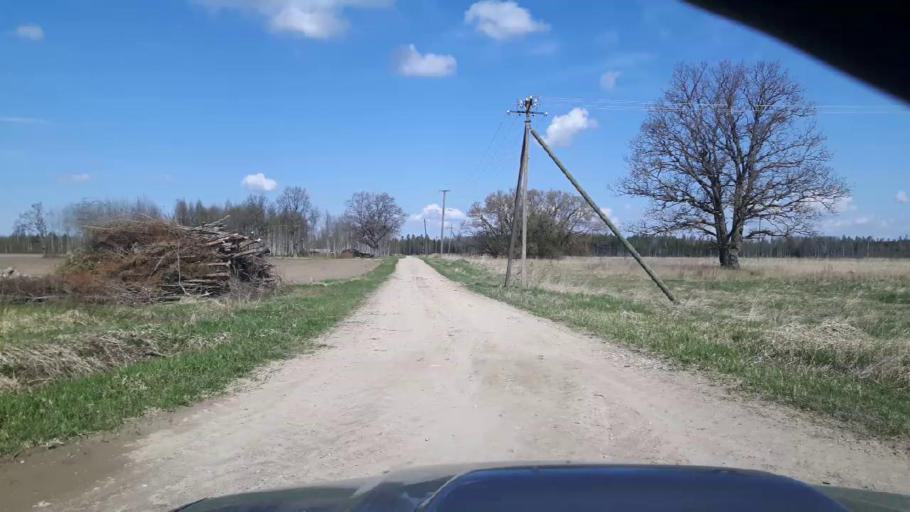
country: EE
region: Paernumaa
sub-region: Vaendra vald (alev)
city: Vandra
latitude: 58.5121
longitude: 25.0452
